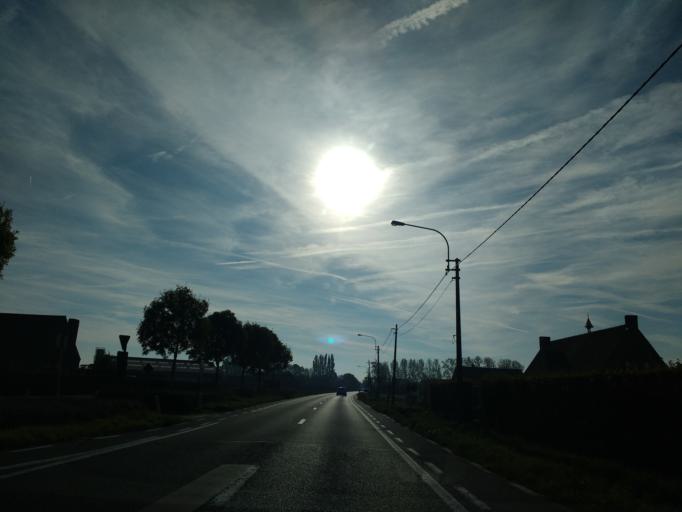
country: BE
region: Flanders
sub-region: Provincie Oost-Vlaanderen
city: Kaprijke
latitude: 51.2464
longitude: 3.6129
